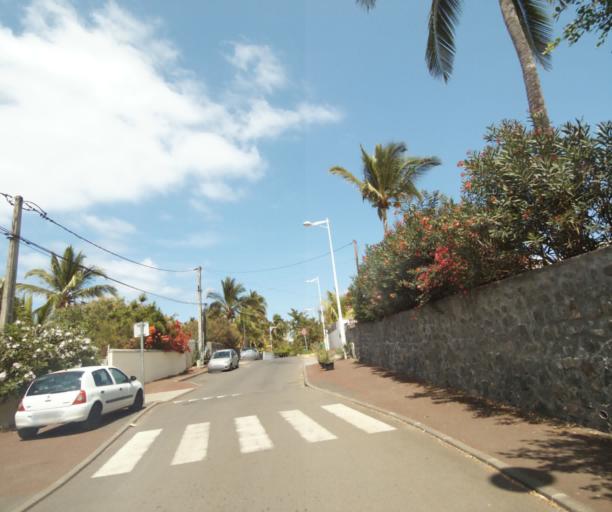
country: RE
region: Reunion
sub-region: Reunion
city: Trois-Bassins
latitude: -21.0918
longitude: 55.2384
